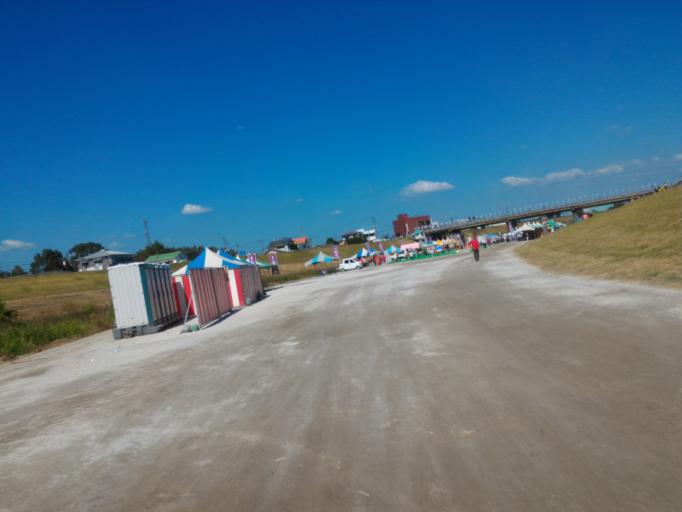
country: JP
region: Kagoshima
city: Kanoya
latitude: 31.3446
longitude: 130.9422
